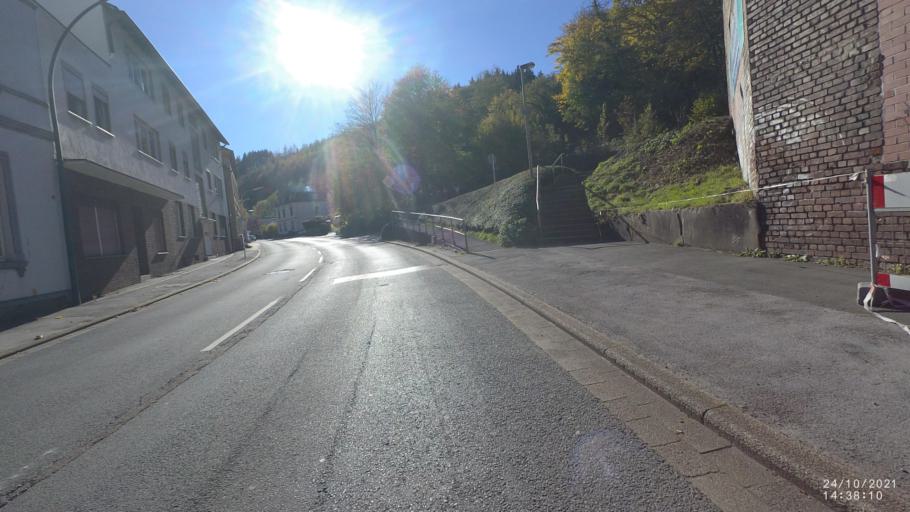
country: DE
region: North Rhine-Westphalia
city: Hemer
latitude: 51.3720
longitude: 7.7522
